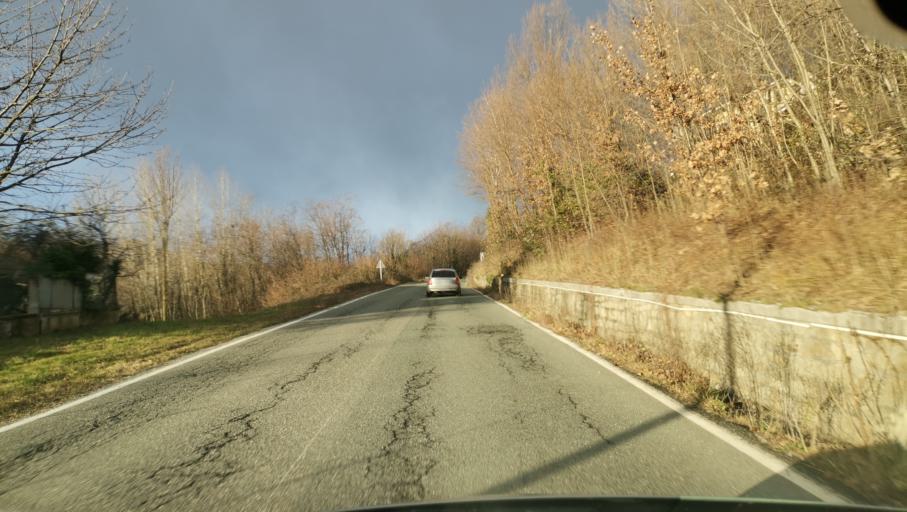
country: IT
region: Piedmont
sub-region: Provincia di Torino
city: Giaveno
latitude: 45.0501
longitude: 7.3319
